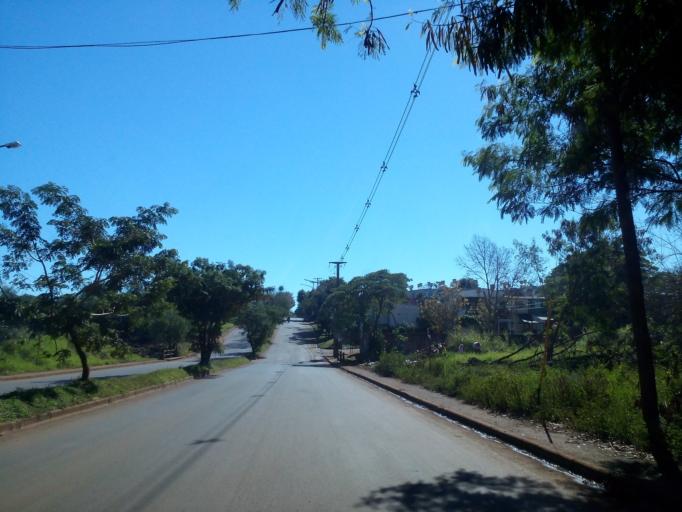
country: AR
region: Misiones
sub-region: Departamento de Capital
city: Posadas
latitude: -27.3897
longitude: -55.9425
